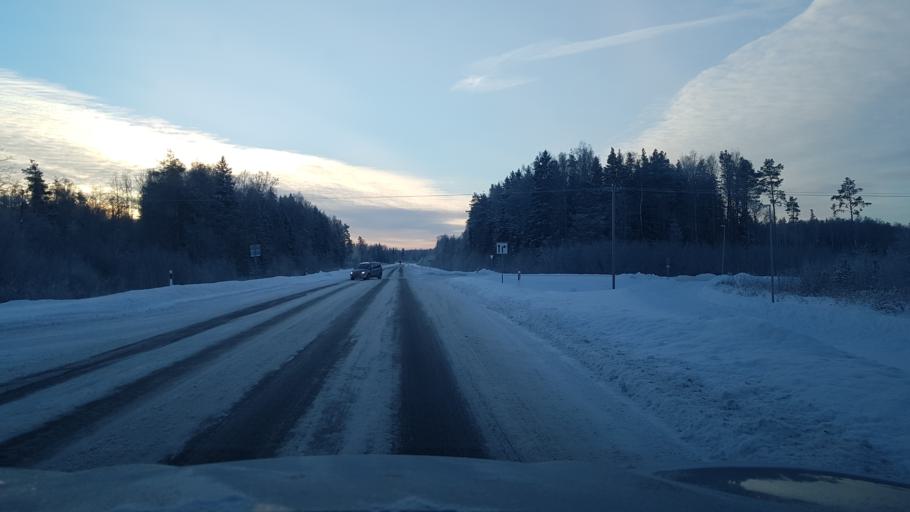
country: EE
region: Ida-Virumaa
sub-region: Johvi vald
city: Johvi
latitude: 59.3601
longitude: 27.4623
